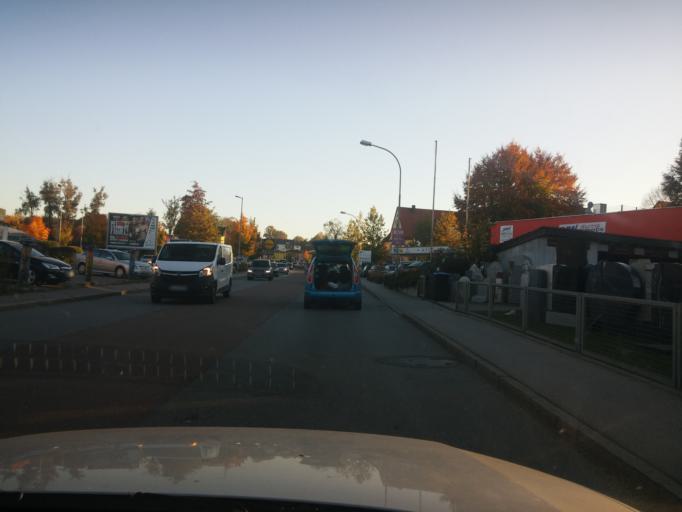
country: DE
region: Bavaria
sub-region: Upper Bavaria
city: Dorfen
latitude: 48.2695
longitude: 12.1547
